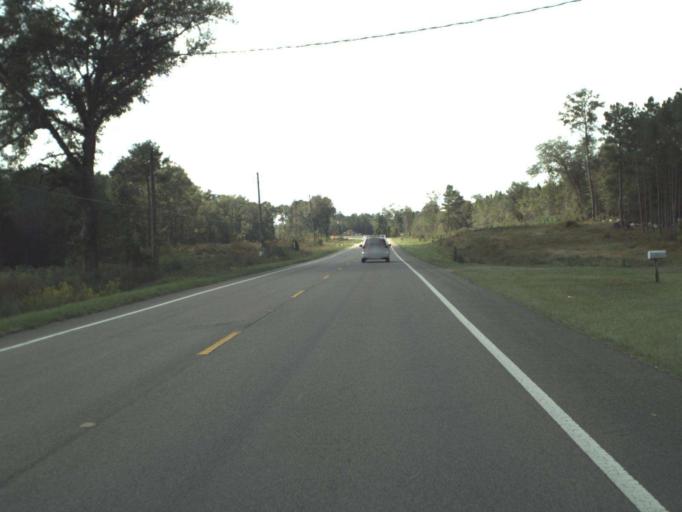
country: US
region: Florida
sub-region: Holmes County
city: Bonifay
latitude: 30.5998
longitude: -85.7569
